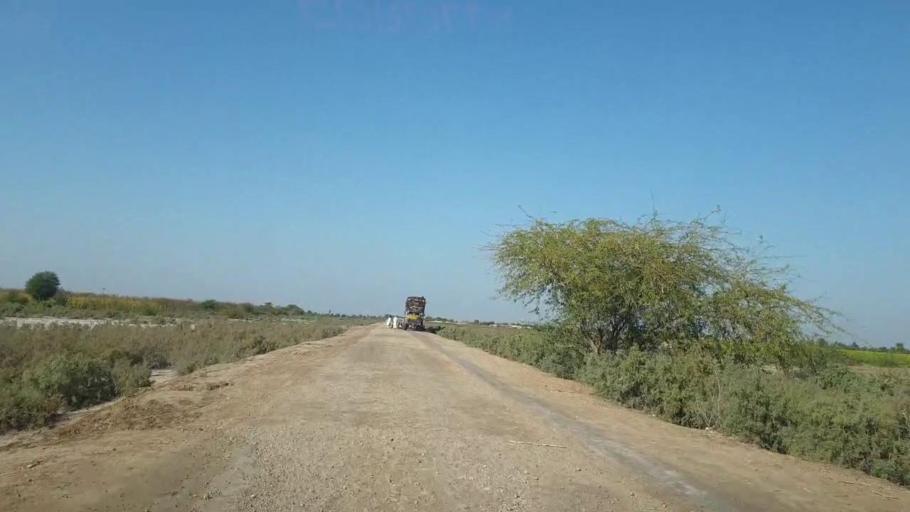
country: PK
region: Sindh
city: Mirpur Khas
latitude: 25.6339
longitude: 69.0589
